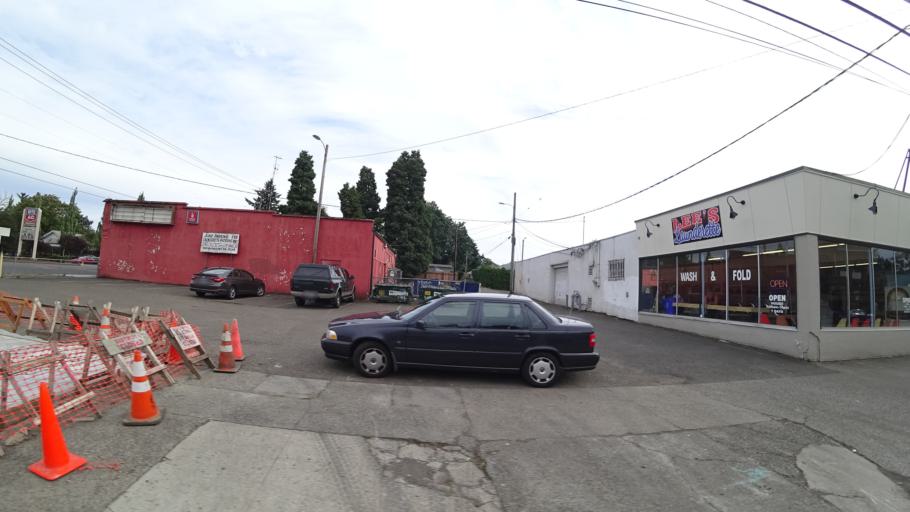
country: US
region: Oregon
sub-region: Multnomah County
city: Portland
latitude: 45.5771
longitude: -122.6877
